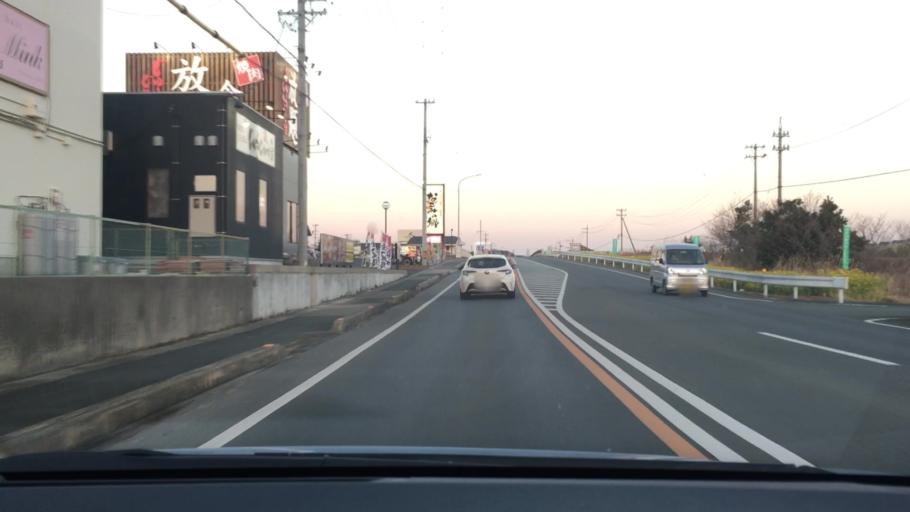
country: JP
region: Aichi
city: Tahara
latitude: 34.6607
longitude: 137.2672
